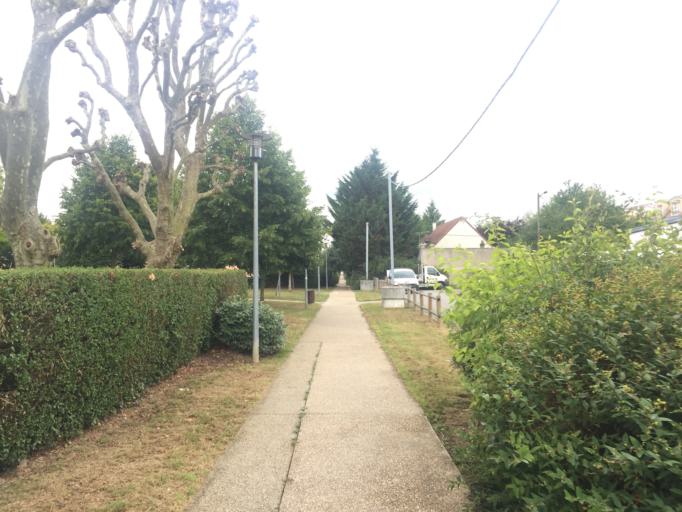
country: FR
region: Ile-de-France
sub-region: Departement des Yvelines
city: Bois-d'Arcy
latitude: 48.7999
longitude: 2.0312
